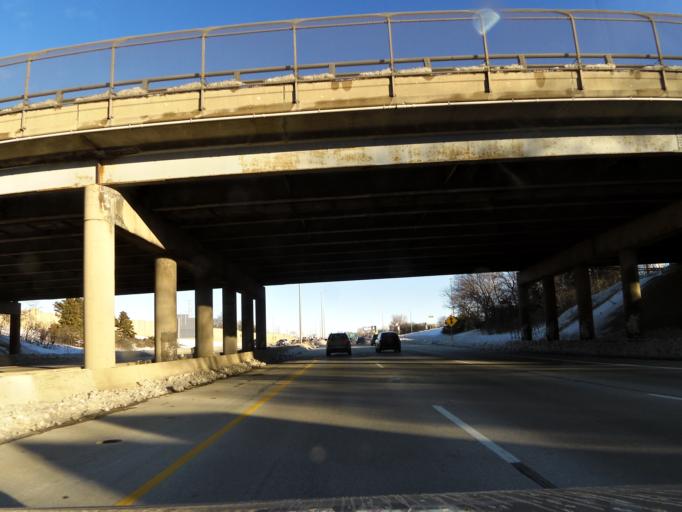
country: US
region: Wisconsin
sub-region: Milwaukee County
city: Greendale
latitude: 42.9623
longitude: -87.9889
